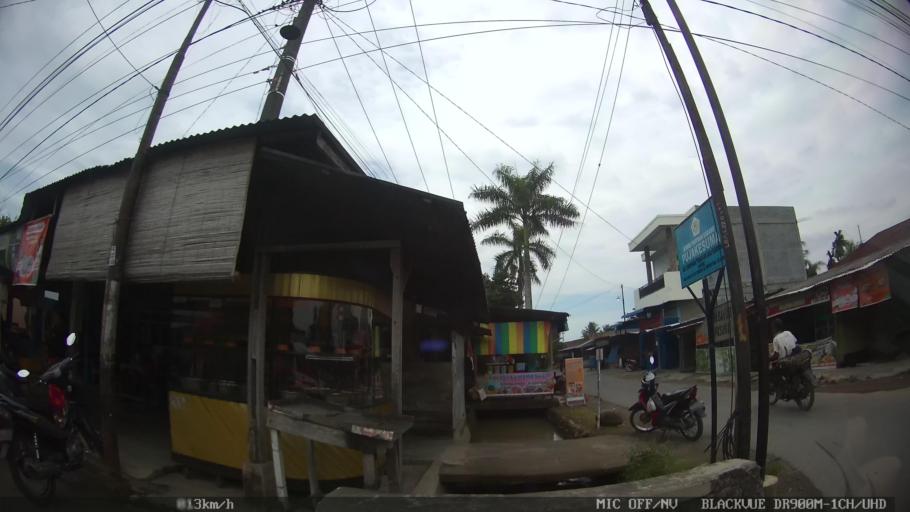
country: ID
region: North Sumatra
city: Binjai
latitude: 3.6288
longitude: 98.5558
